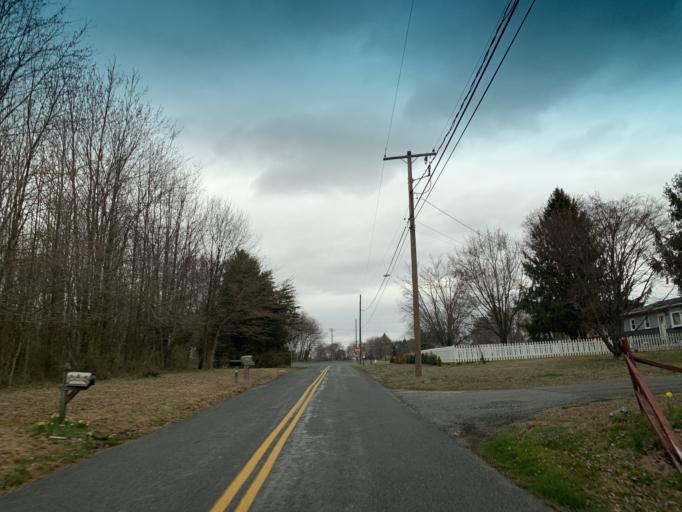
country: US
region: Maryland
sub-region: Harford County
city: Aberdeen
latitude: 39.5773
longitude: -76.1981
